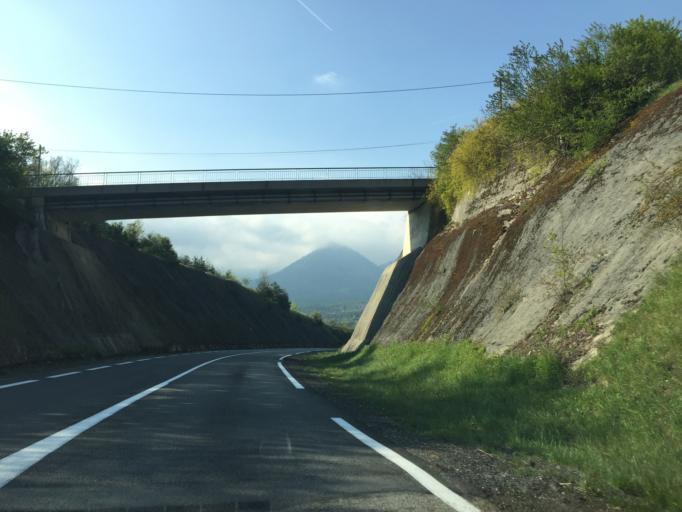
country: FR
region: Rhone-Alpes
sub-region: Departement de l'Isere
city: Mens
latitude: 44.7968
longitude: 5.6359
